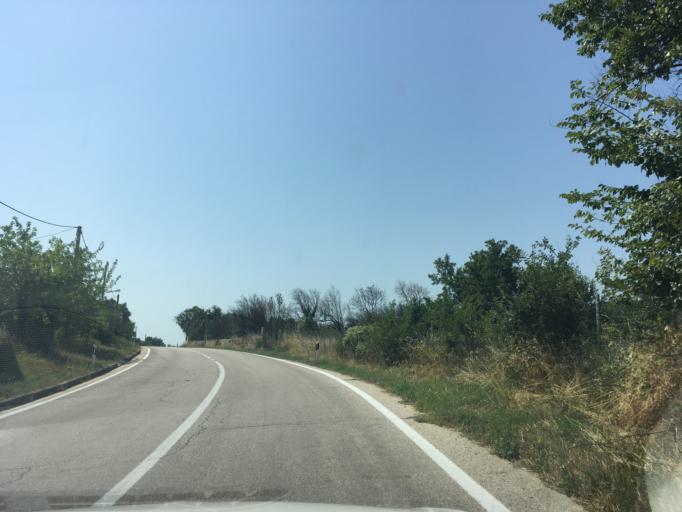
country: HR
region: Zadarska
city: Benkovac
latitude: 43.9959
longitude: 15.6847
